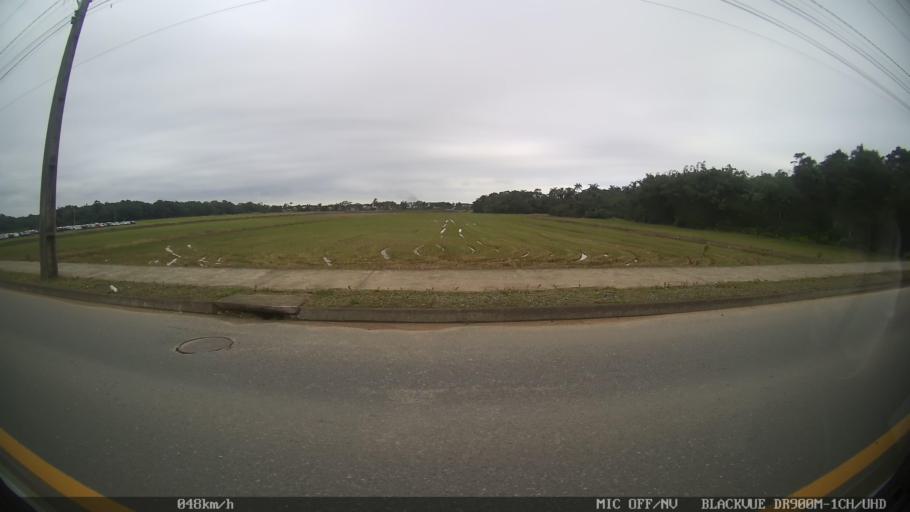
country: BR
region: Santa Catarina
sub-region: Joinville
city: Joinville
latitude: -26.2782
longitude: -48.9210
